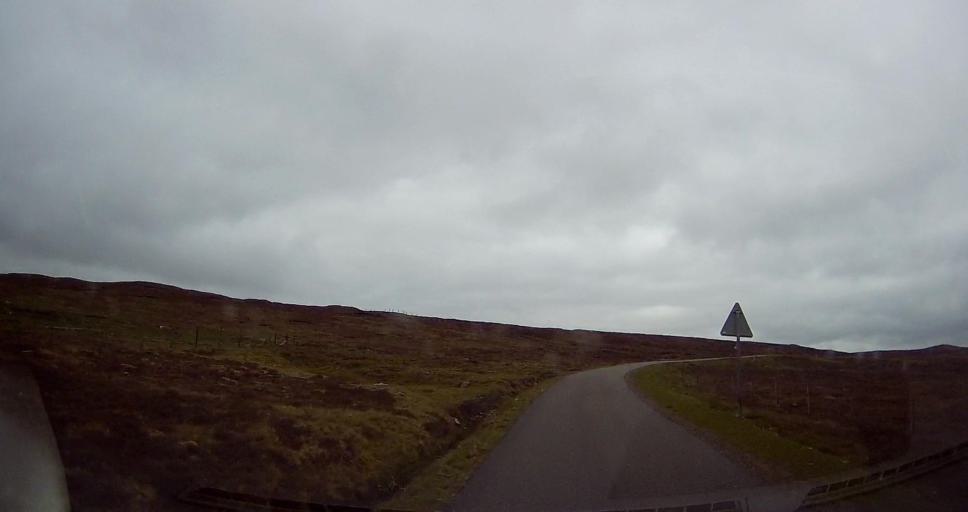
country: GB
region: Scotland
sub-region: Shetland Islands
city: Lerwick
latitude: 60.3119
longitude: -1.3403
